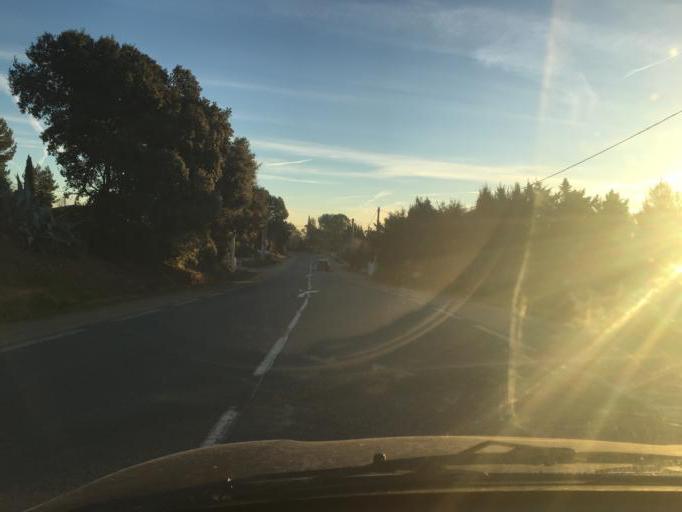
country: FR
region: Provence-Alpes-Cote d'Azur
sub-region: Departement du Var
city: Taradeau
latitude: 43.4488
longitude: 6.4388
